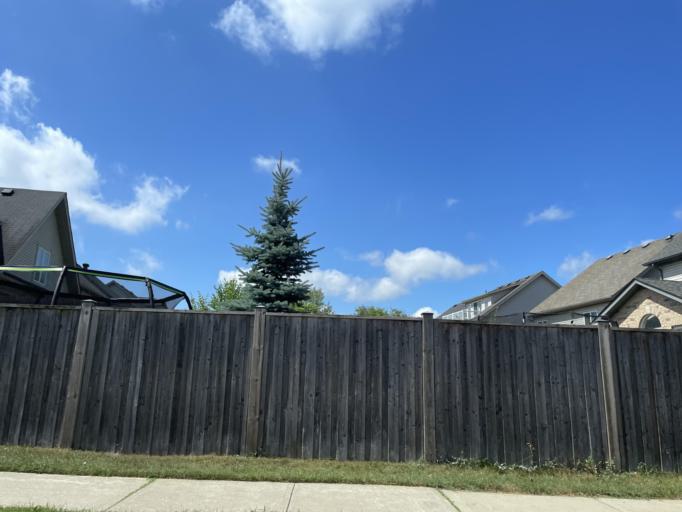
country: CA
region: Ontario
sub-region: Wellington County
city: Guelph
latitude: 43.5166
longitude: -80.1899
